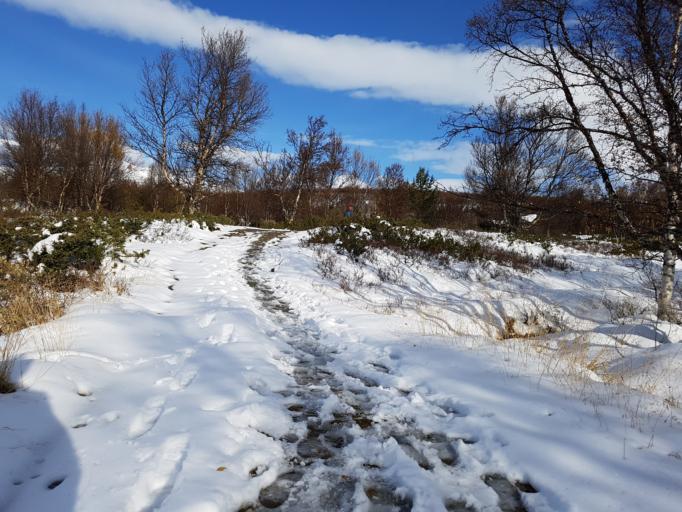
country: NO
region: Oppland
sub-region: Sel
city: Otta
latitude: 61.8257
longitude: 9.6810
